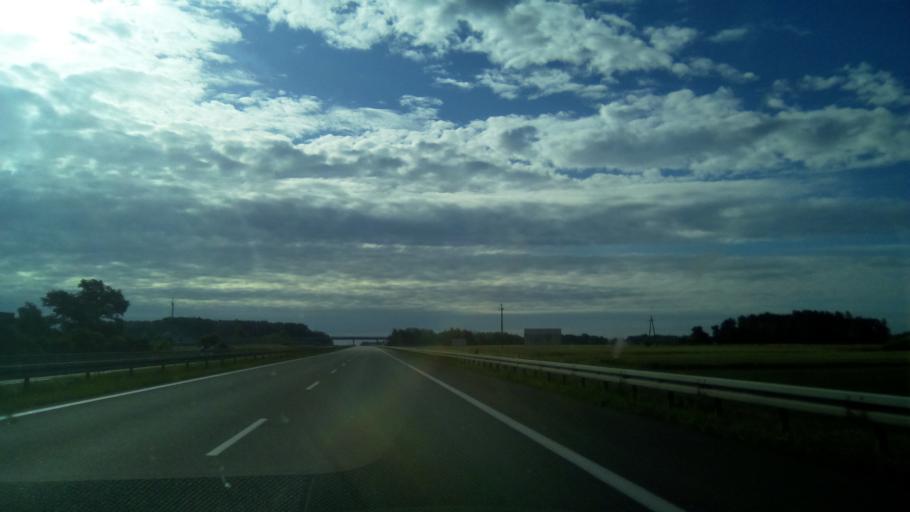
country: PL
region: Greater Poland Voivodeship
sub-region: Powiat koninski
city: Stare Miasto
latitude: 52.1718
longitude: 18.1569
